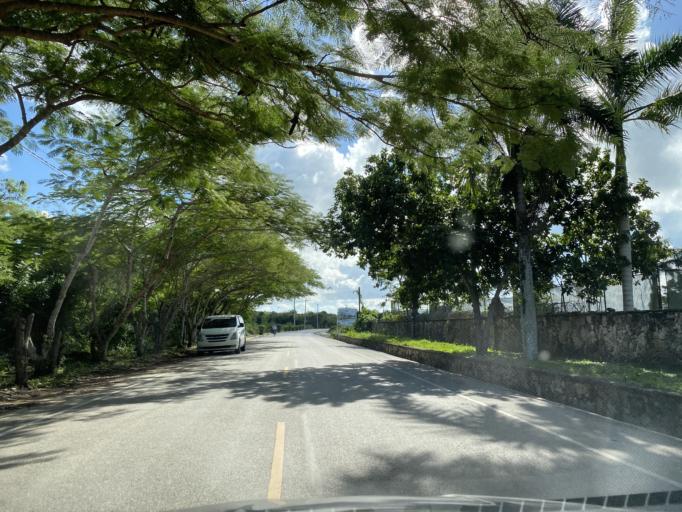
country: DO
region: La Altagracia
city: San Rafael del Yuma
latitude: 18.3431
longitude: -68.8152
